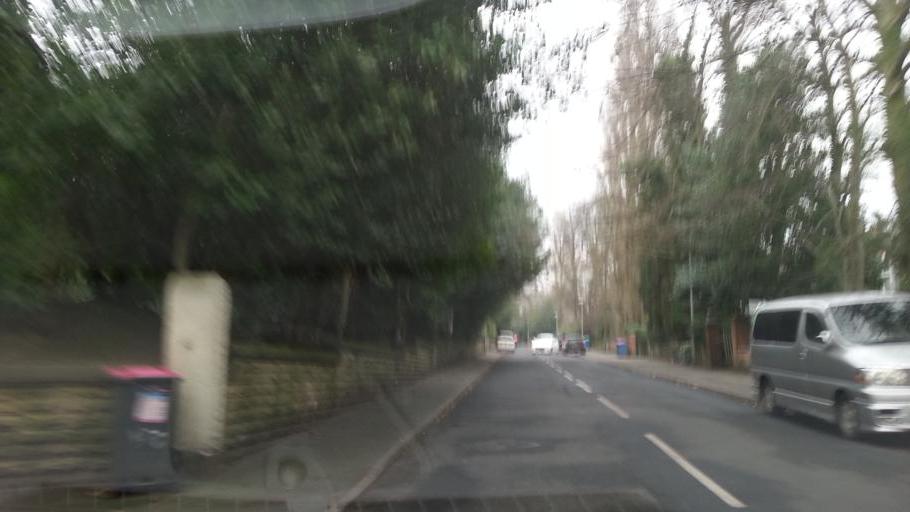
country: GB
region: England
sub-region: Manchester
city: Crumpsall
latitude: 53.5107
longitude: -2.2616
